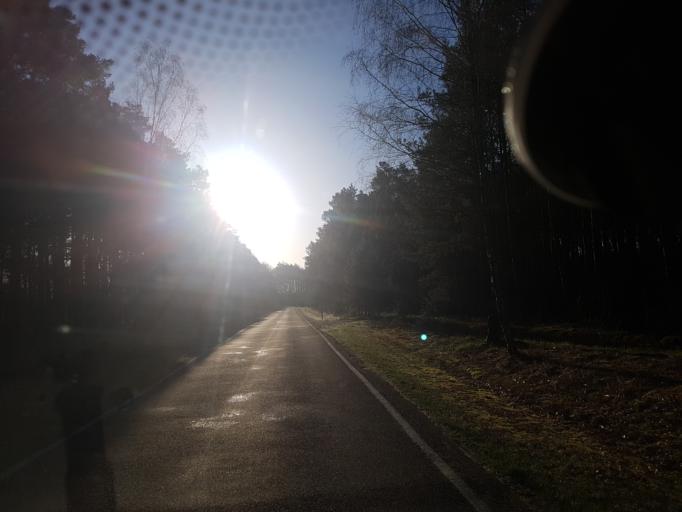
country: DE
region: Brandenburg
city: Lieberose
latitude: 52.0379
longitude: 14.3155
